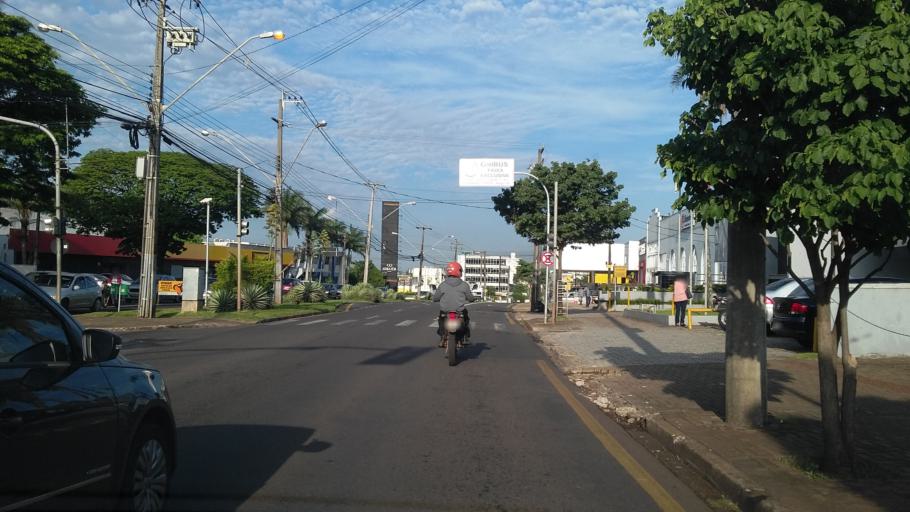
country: BR
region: Parana
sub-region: Londrina
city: Londrina
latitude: -23.3003
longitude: -51.1867
